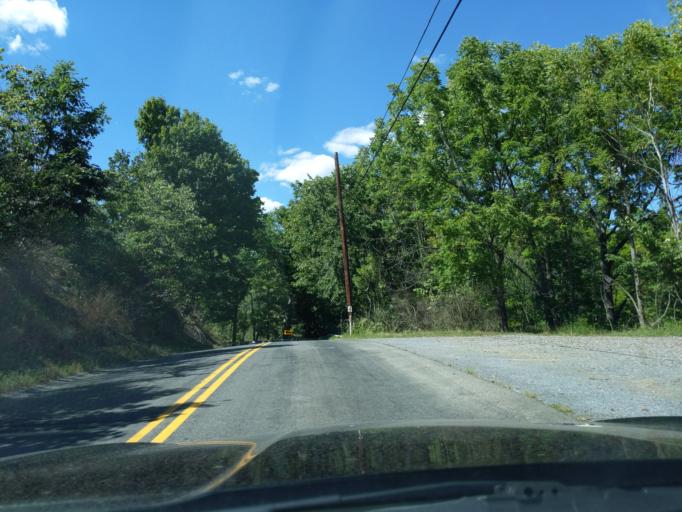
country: US
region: Pennsylvania
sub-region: Blair County
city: Williamsburg
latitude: 40.4745
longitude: -78.2823
